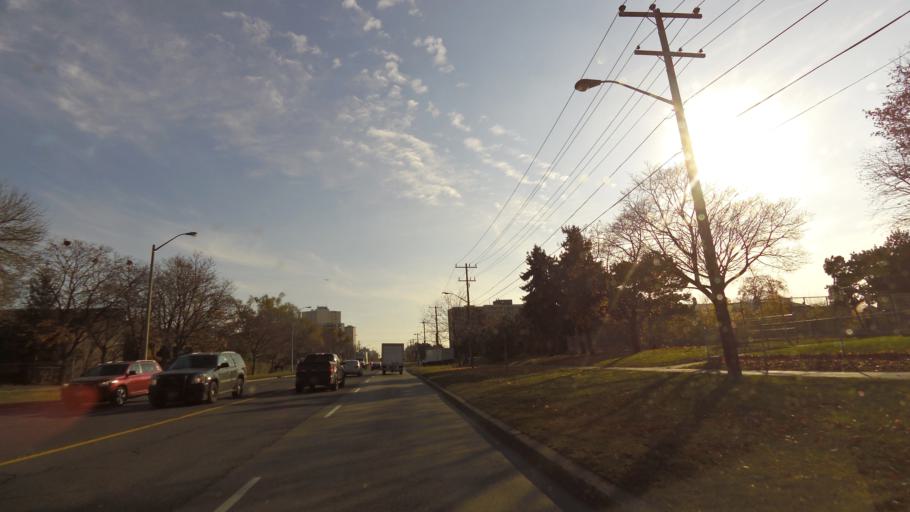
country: CA
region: Ontario
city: Concord
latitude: 43.7649
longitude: -79.5196
